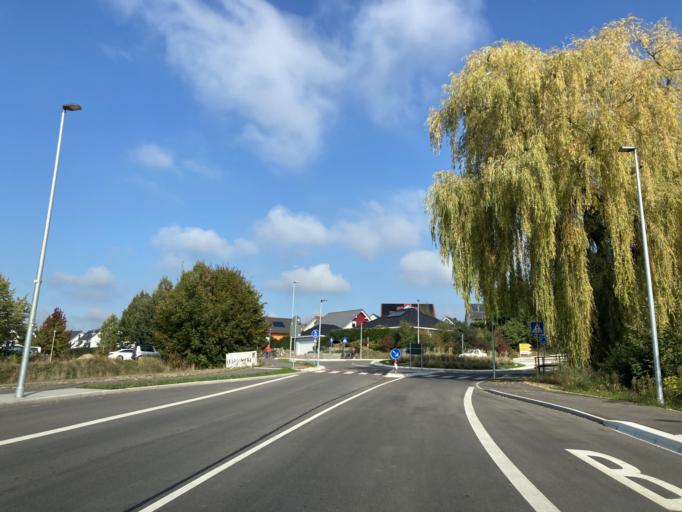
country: DE
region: Baden-Wuerttemberg
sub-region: Freiburg Region
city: Mullheim
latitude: 47.8105
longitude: 7.6371
